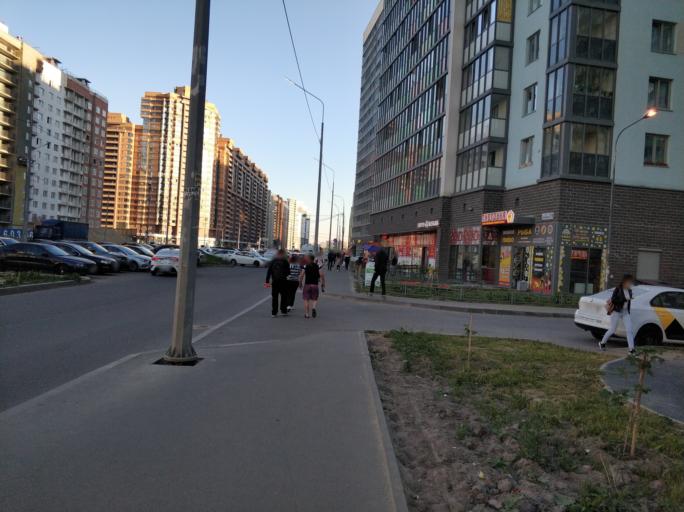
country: RU
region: Leningrad
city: Murino
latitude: 60.0597
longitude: 30.4301
